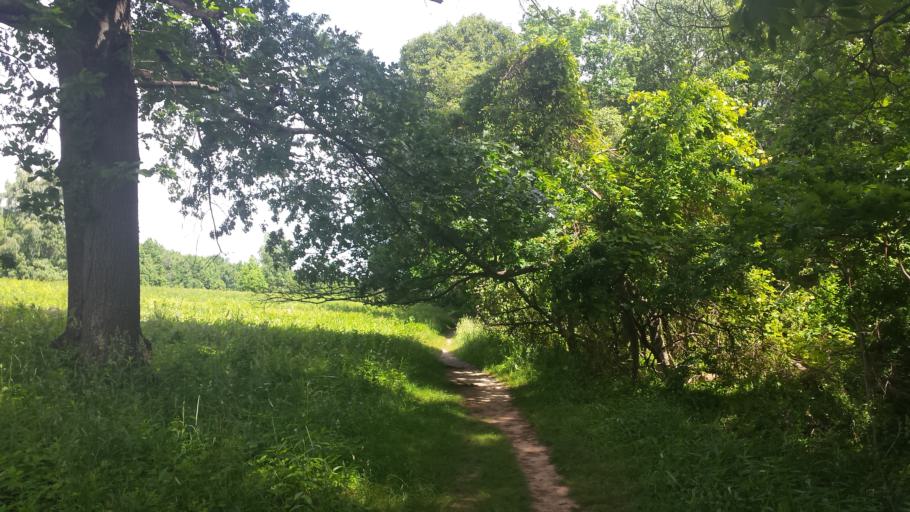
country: US
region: New York
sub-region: Westchester County
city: Harrison
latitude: 40.9511
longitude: -73.7020
